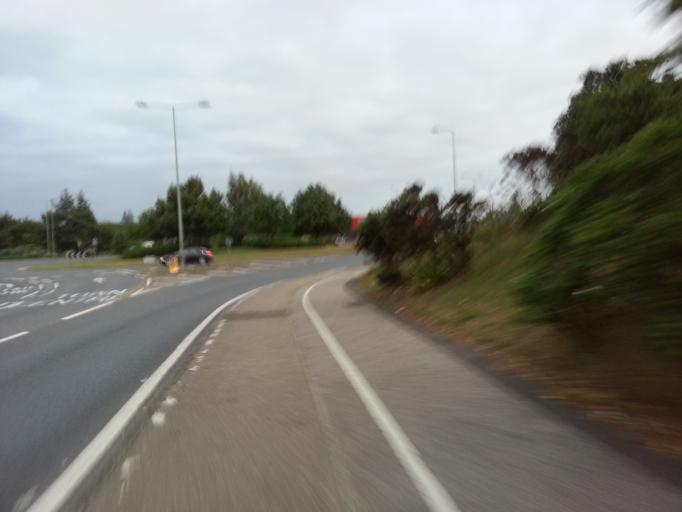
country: GB
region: England
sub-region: Suffolk
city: Bramford
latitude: 52.0836
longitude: 1.1162
